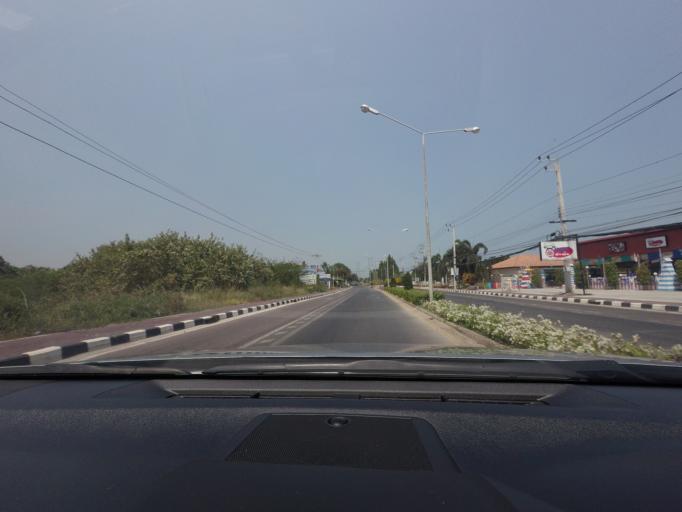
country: TH
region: Phetchaburi
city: Cha-am
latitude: 12.8179
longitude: 99.9822
